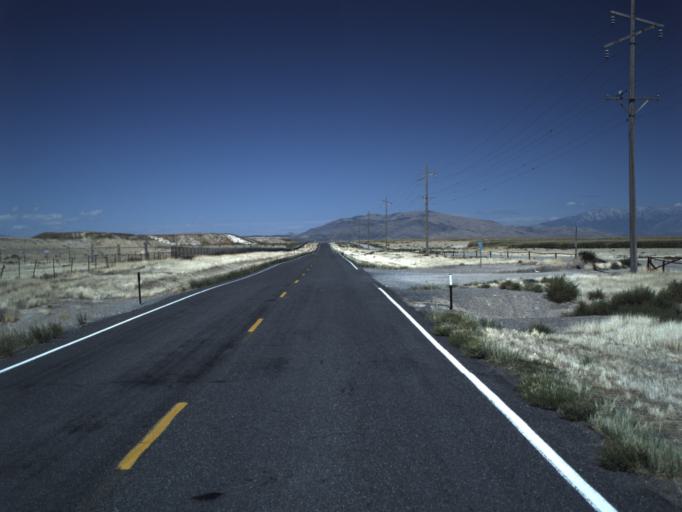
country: US
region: Utah
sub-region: Utah County
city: Genola
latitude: 40.0240
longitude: -111.9583
